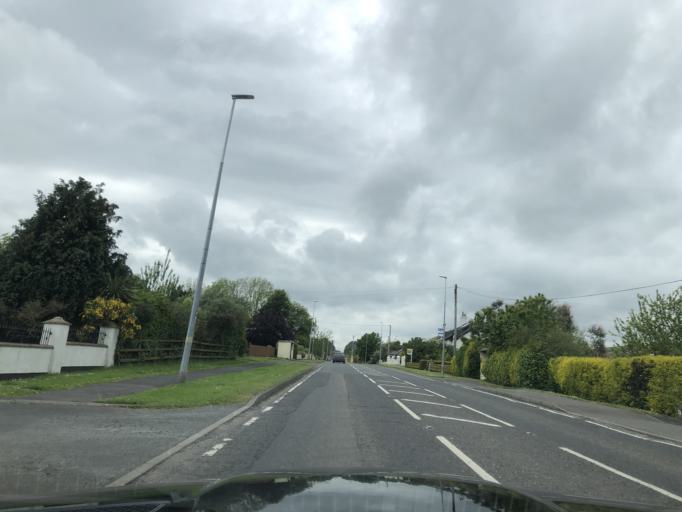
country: GB
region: Northern Ireland
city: Crossgar
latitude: 54.3658
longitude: -5.7798
